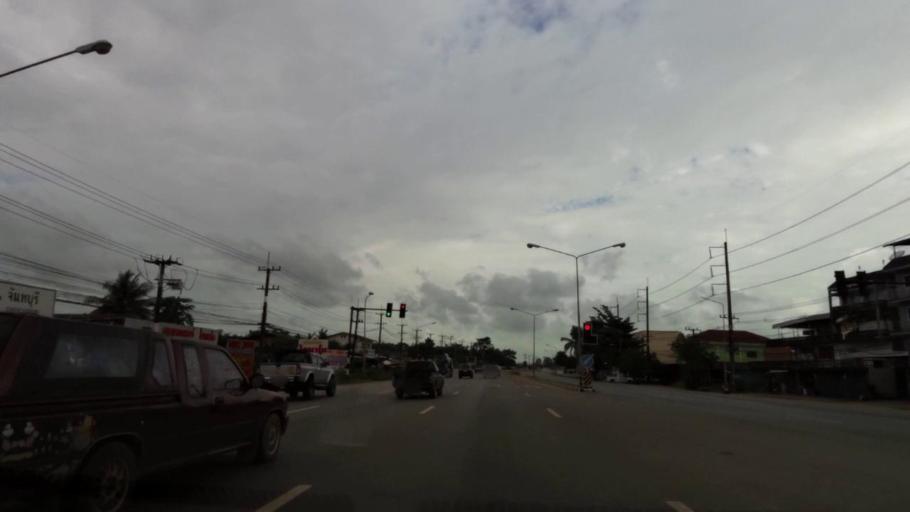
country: TH
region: Chanthaburi
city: Tha Mai
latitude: 12.7222
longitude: 101.9587
